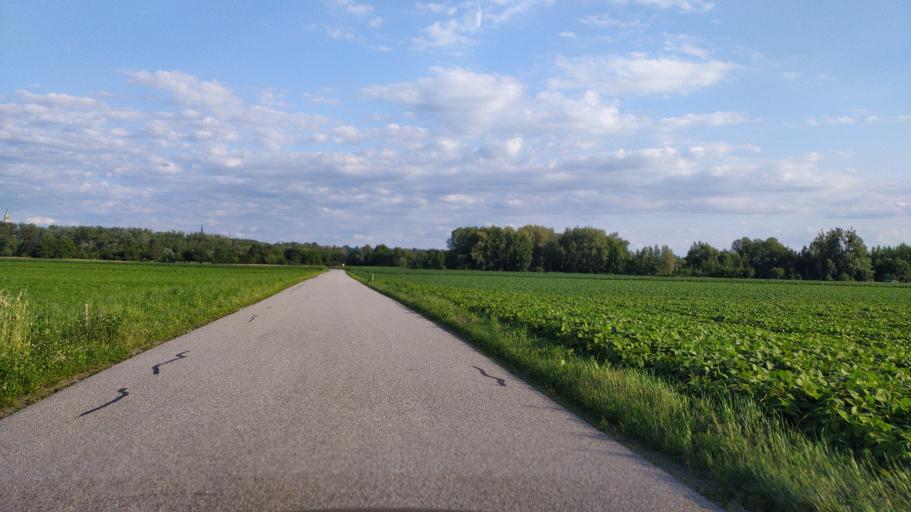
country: AT
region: Lower Austria
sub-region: Politischer Bezirk Amstetten
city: Strengberg
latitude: 48.1815
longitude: 14.6991
